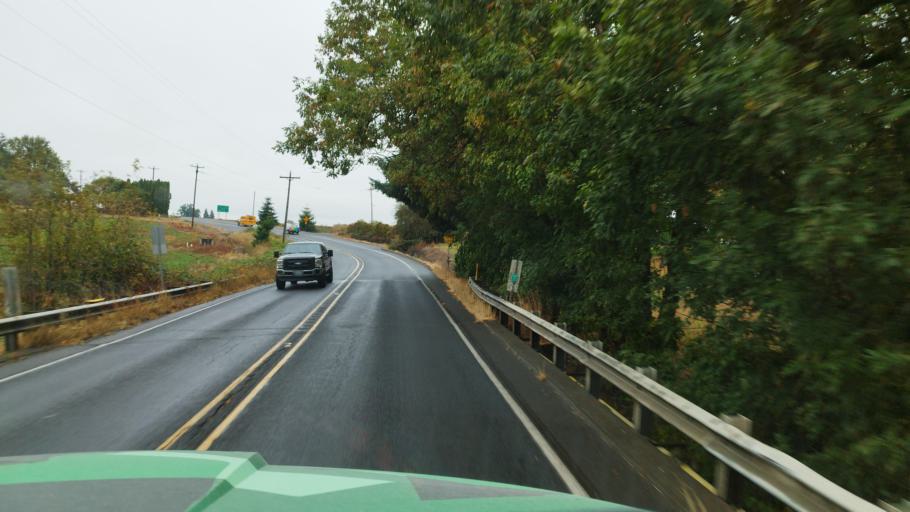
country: US
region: Oregon
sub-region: Washington County
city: Cornelius
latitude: 45.5550
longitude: -123.0627
